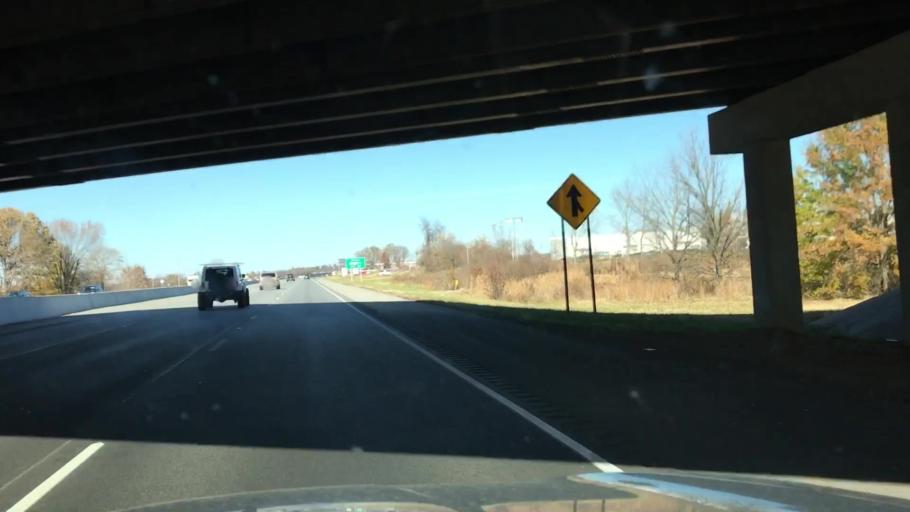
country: US
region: Arkansas
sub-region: Benton County
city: Lowell
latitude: 36.2835
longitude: -94.1564
